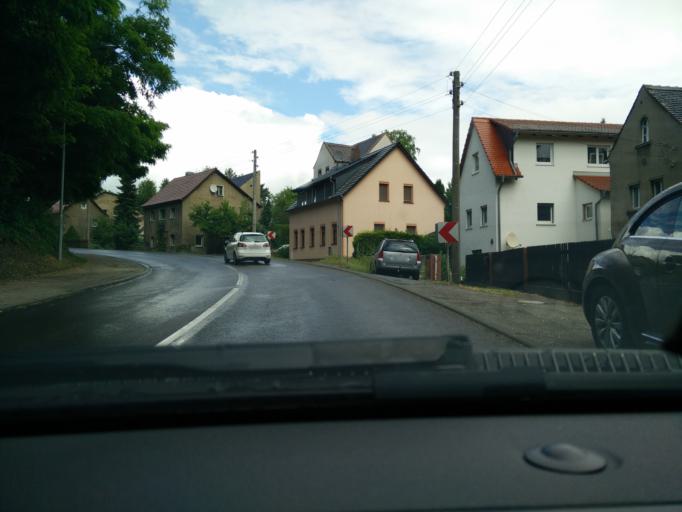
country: DE
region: Saxony
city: Grimma
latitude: 51.2446
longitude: 12.7312
